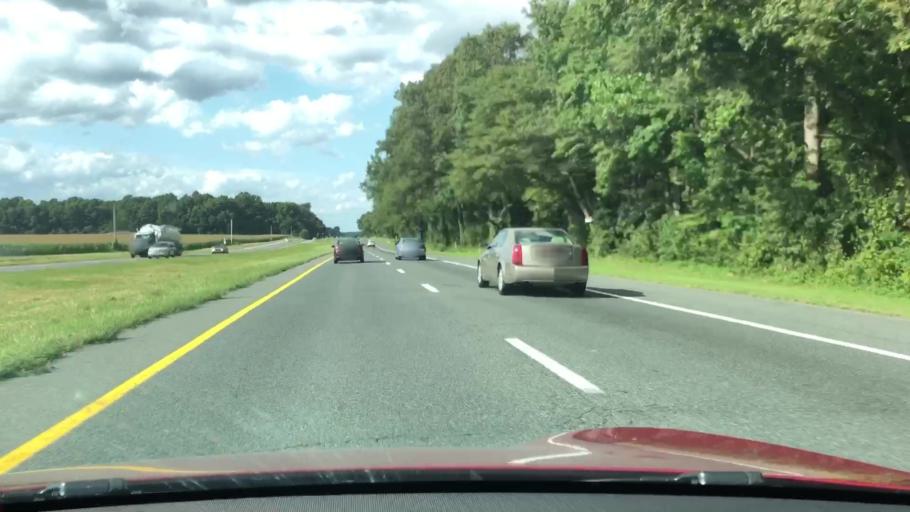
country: US
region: Delaware
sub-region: Sussex County
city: Bridgeville
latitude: 38.7648
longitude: -75.5929
